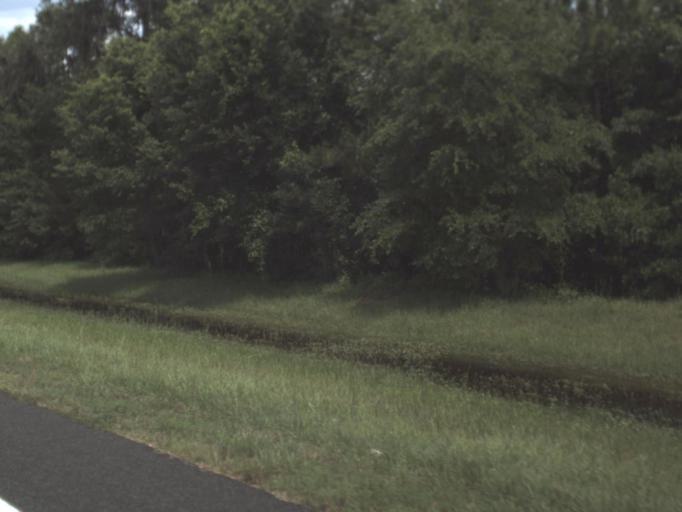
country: US
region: Florida
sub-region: Alachua County
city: Hawthorne
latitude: 29.6033
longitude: -82.2085
